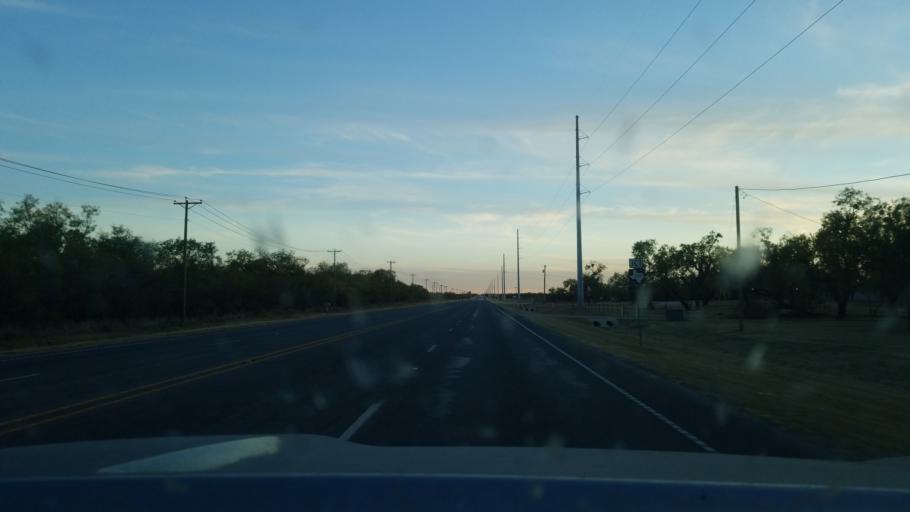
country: US
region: Texas
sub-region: Stephens County
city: Breckenridge
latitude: 32.7353
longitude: -98.9026
